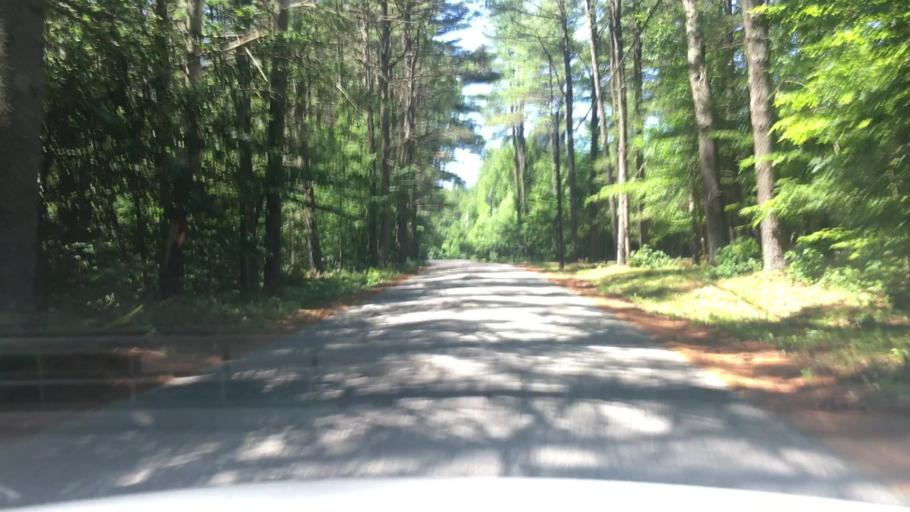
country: US
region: New Hampshire
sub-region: Merrimack County
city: Hopkinton
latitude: 43.2300
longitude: -71.6590
